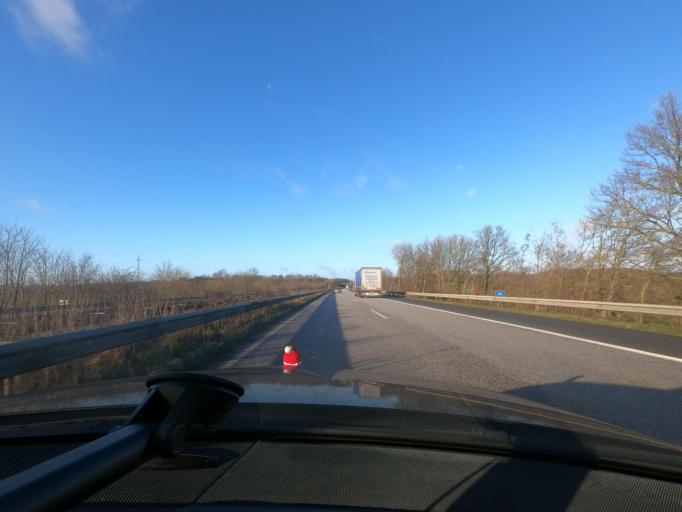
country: DE
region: Schleswig-Holstein
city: Dannewerk
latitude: 54.5014
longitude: 9.5094
